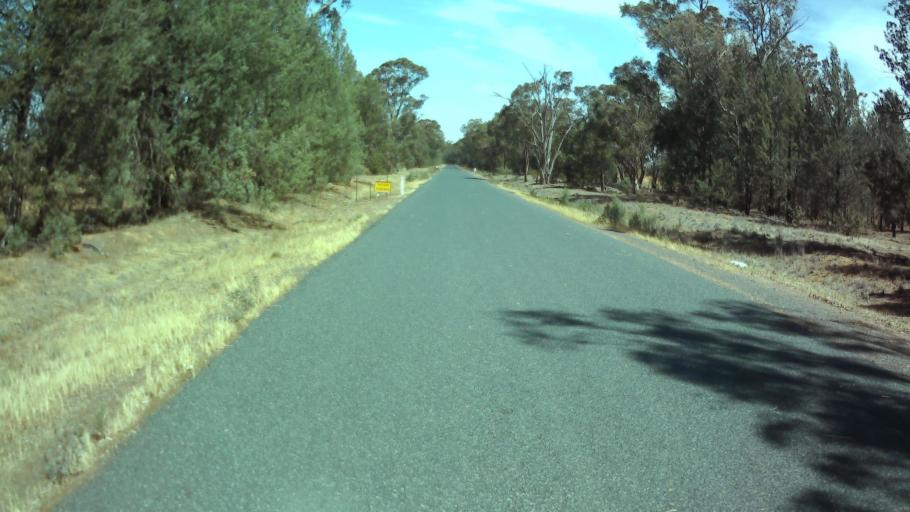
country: AU
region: New South Wales
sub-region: Weddin
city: Grenfell
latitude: -34.0652
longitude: 148.1360
